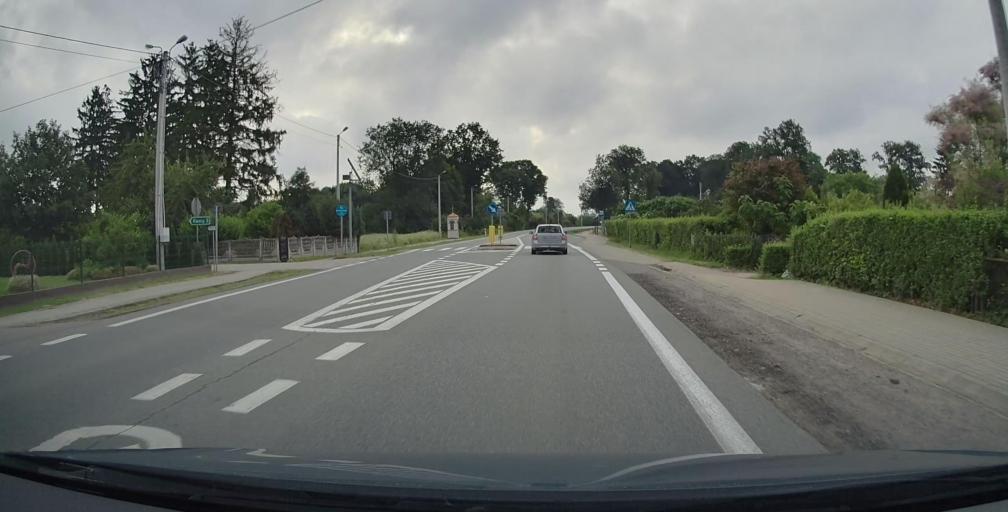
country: PL
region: Lublin Voivodeship
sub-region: Powiat lukowski
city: Trzebieszow
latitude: 52.0689
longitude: 22.5239
